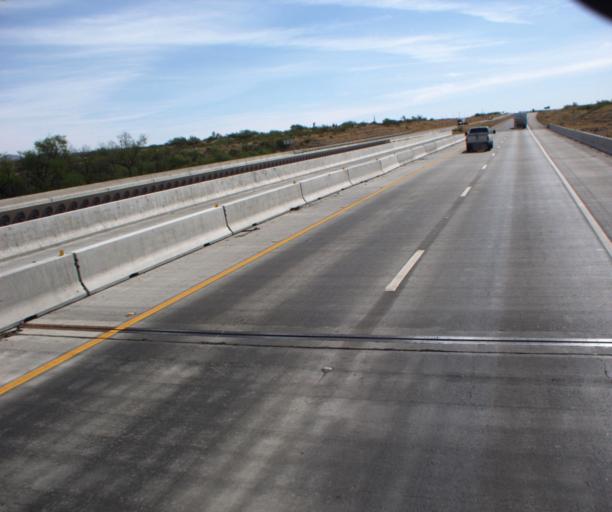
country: US
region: Arizona
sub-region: Cochise County
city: Mescal
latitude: 31.9857
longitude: -110.5678
